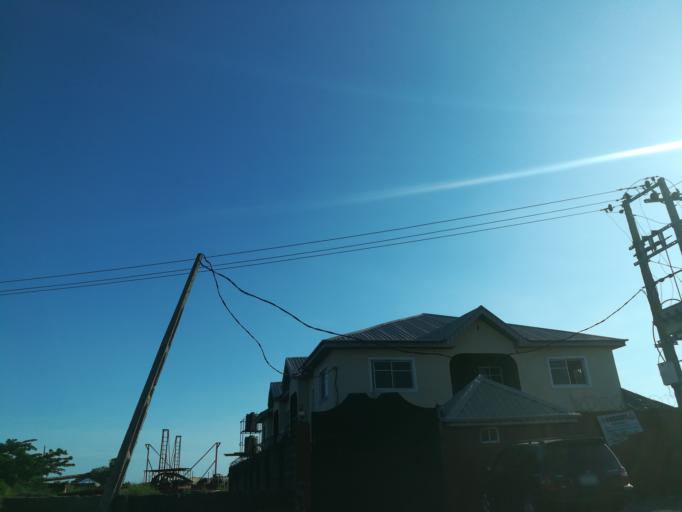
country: NG
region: Lagos
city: Ebute Ikorodu
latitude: 6.5404
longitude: 3.5490
